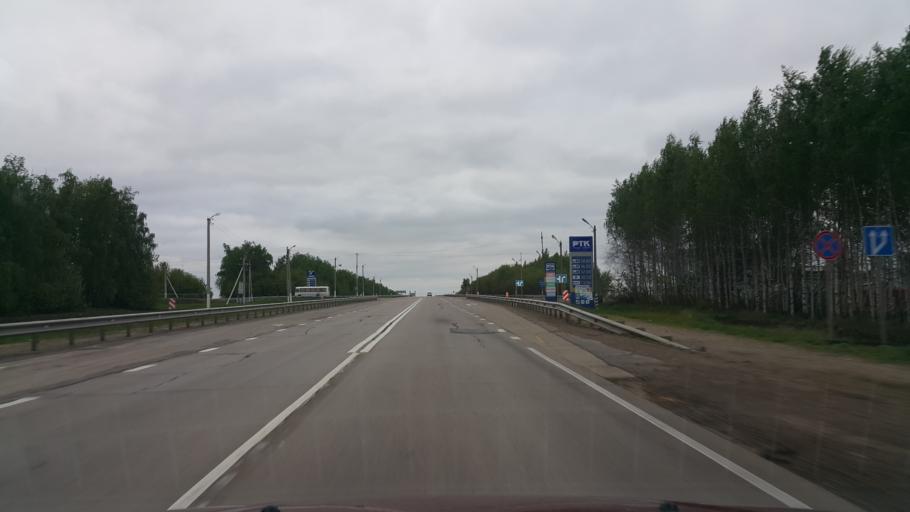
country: RU
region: Tambov
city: Znamenka
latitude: 52.4014
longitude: 41.3915
